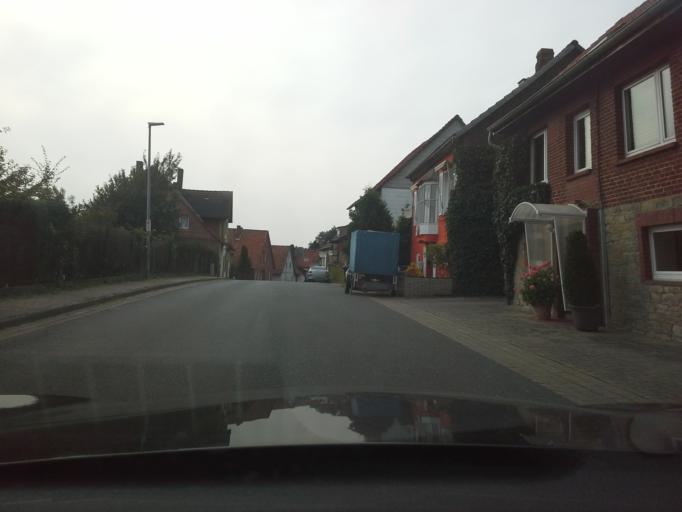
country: DE
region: Lower Saxony
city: Barsinghausen
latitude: 52.2576
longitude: 9.4540
